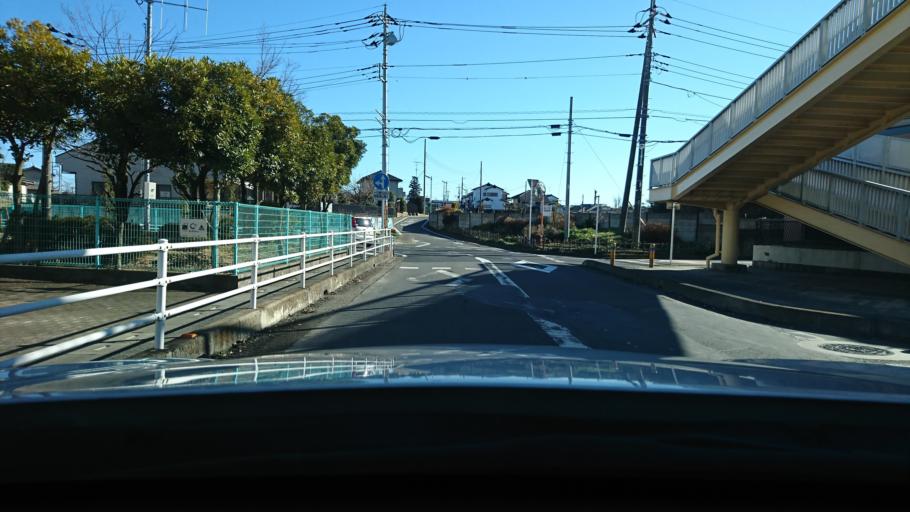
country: JP
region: Saitama
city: Kamifukuoka
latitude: 35.8871
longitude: 139.5170
